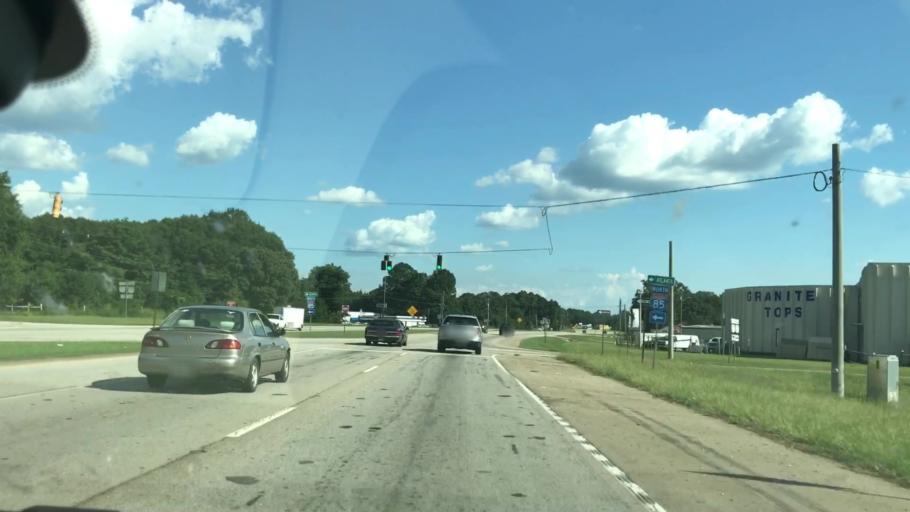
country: US
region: Georgia
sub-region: Troup County
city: La Grange
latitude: 32.9994
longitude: -85.0118
